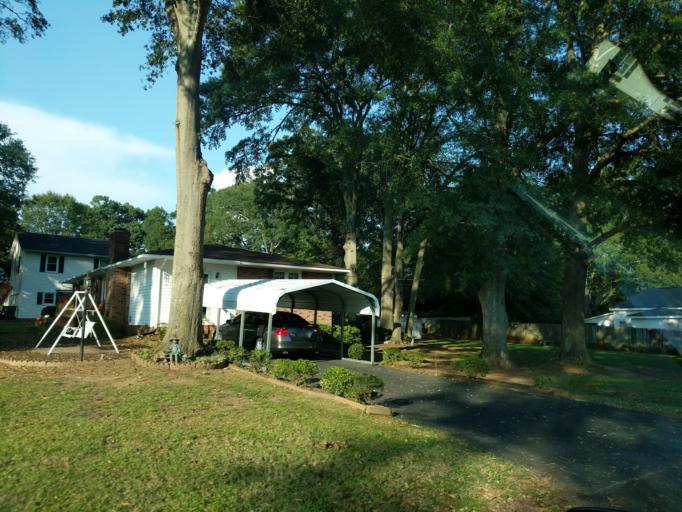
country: US
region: South Carolina
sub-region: Anderson County
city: Williamston
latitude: 34.6457
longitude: -82.4676
